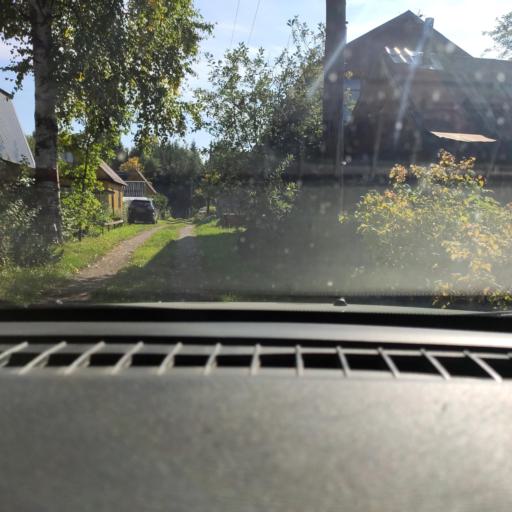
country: RU
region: Perm
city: Novyye Lyady
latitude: 58.0613
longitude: 56.5815
